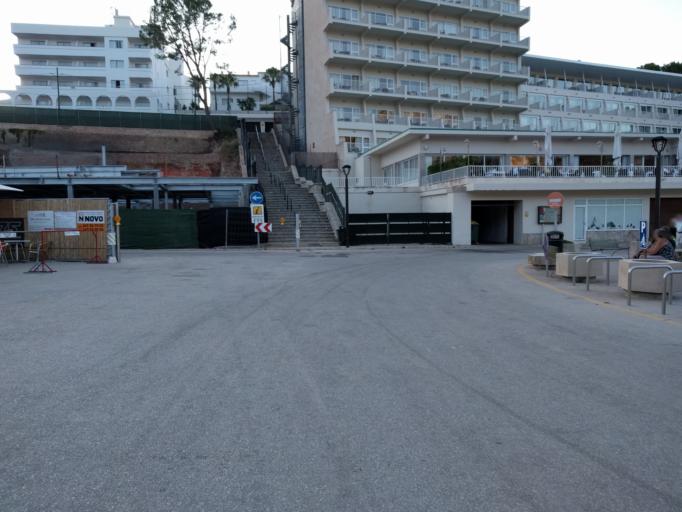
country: ES
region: Balearic Islands
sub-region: Illes Balears
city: Pollenca
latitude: 39.9197
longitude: 3.0570
